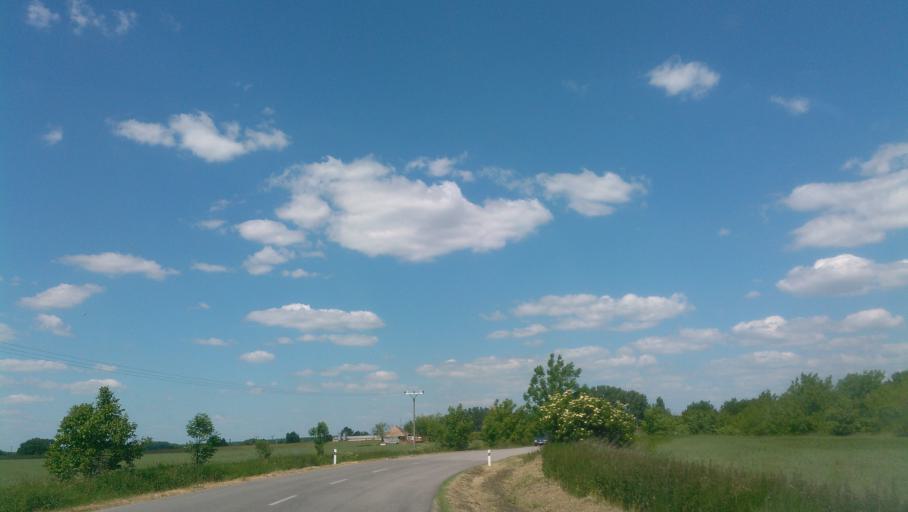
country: SK
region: Nitriansky
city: Kolarovo
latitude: 47.9006
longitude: 17.9719
